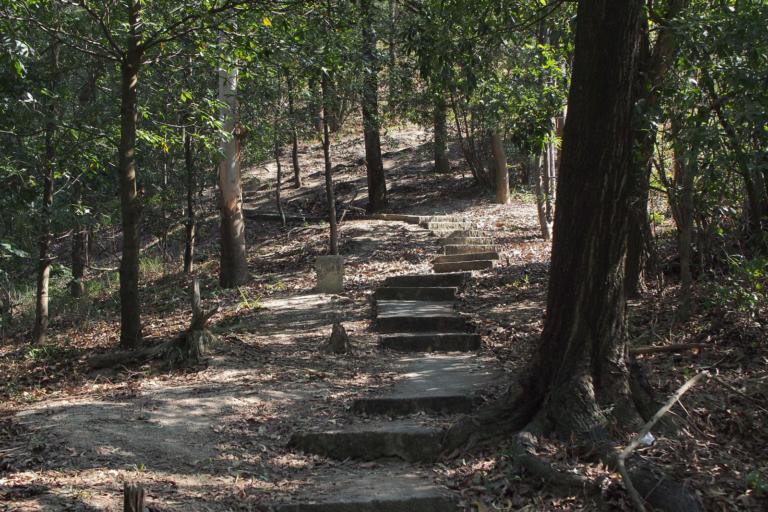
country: CN
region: Guangdong
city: Huancheng
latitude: 22.4643
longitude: 113.4139
